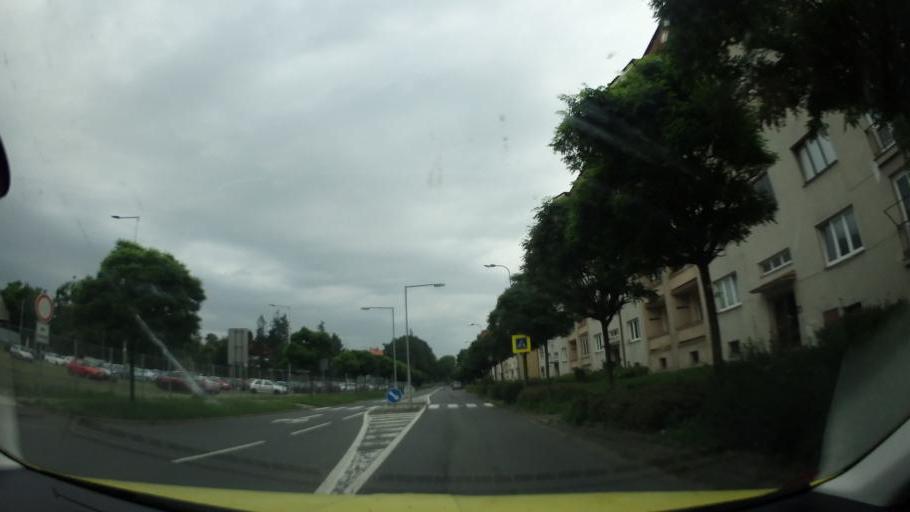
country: CZ
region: Olomoucky
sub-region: Okres Prerov
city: Hranice
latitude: 49.5488
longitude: 17.7286
